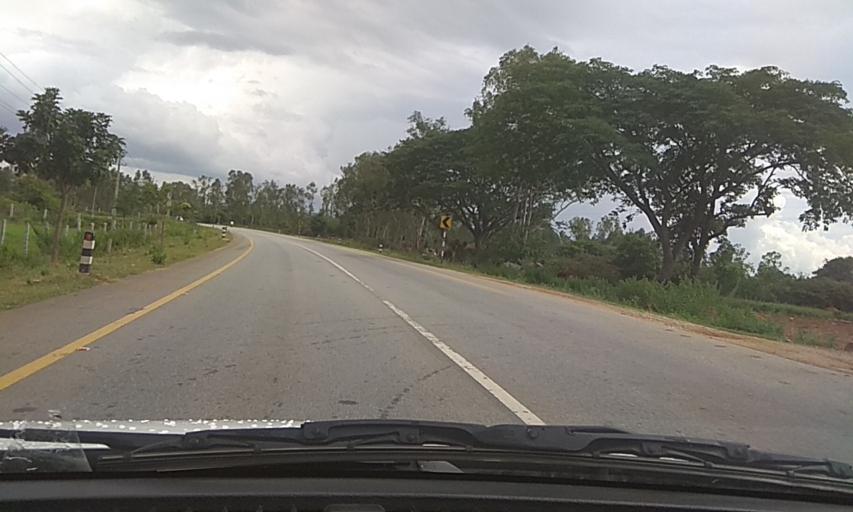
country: IN
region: Karnataka
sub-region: Tumkur
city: Kunigal
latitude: 12.9143
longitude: 77.0323
